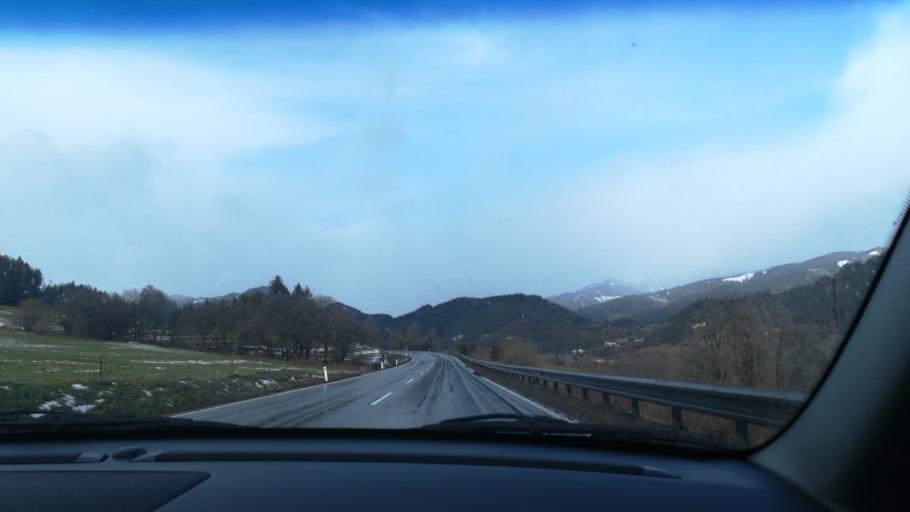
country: AT
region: Styria
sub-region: Politischer Bezirk Murtal
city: Sankt Peter ob Judenburg
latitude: 47.1912
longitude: 14.5836
